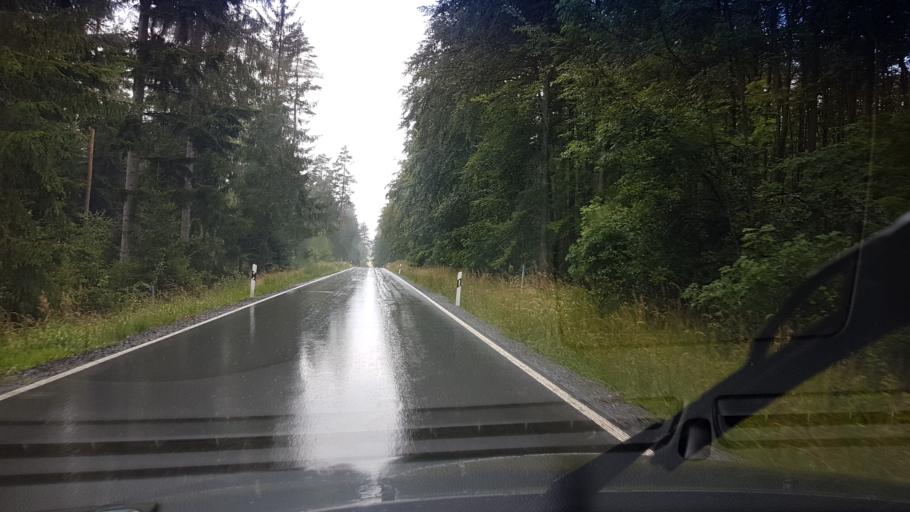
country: DE
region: Bavaria
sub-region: Upper Franconia
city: Arzberg
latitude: 50.0459
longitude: 12.2095
